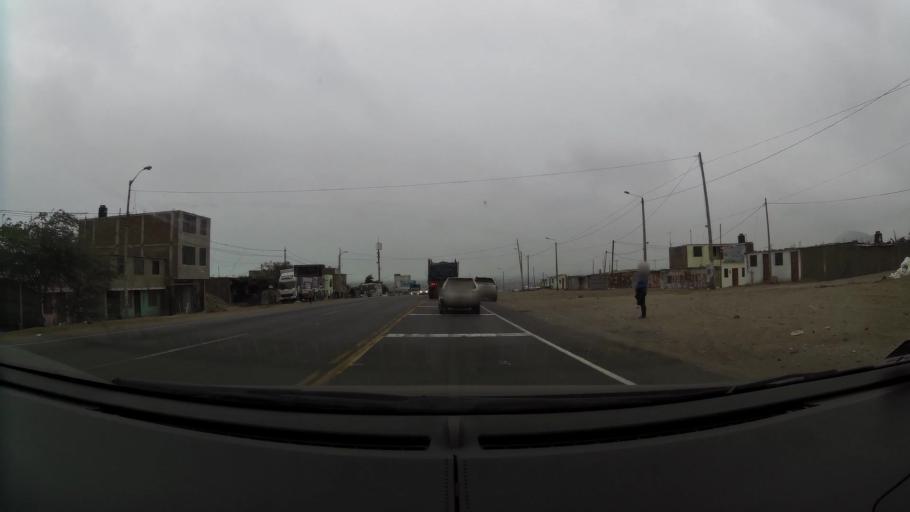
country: PE
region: La Libertad
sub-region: Provincia de Trujillo
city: Moche
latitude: -8.1839
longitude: -78.9853
